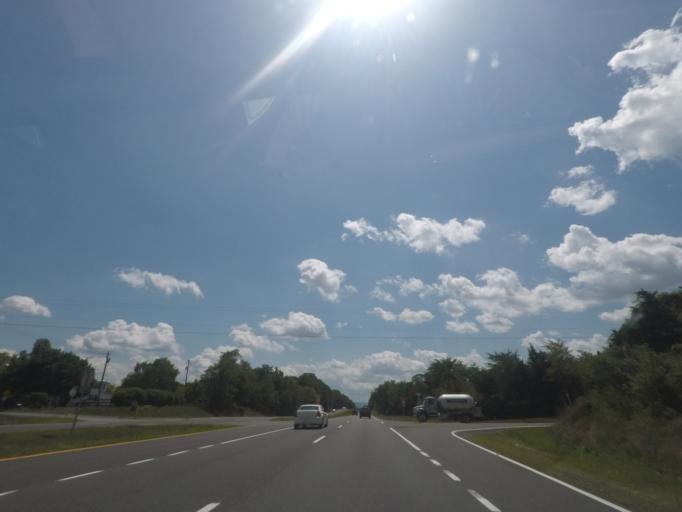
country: US
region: Virginia
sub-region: City of Winchester
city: Winchester
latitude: 39.1089
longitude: -78.1163
